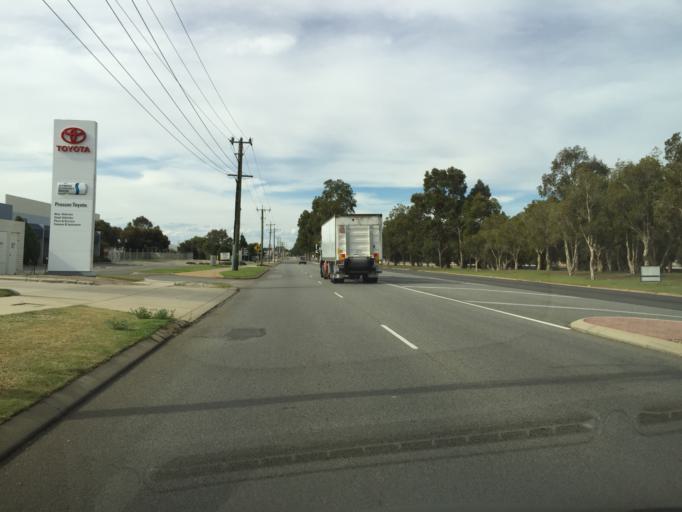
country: AU
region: Western Australia
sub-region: Canning
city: Willetton
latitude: -32.0653
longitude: 115.9008
